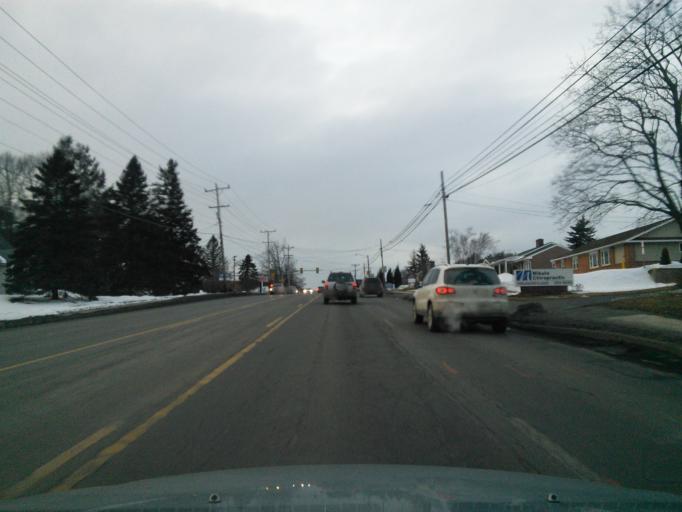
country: US
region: Pennsylvania
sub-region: Centre County
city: State College
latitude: 40.8045
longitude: -77.8858
